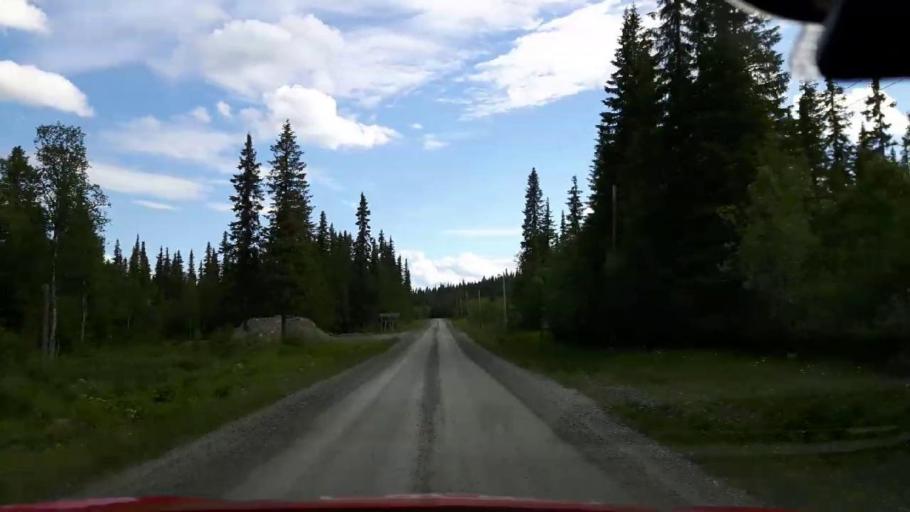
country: SE
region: Jaemtland
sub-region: Krokoms Kommun
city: Valla
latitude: 63.8239
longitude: 14.0408
